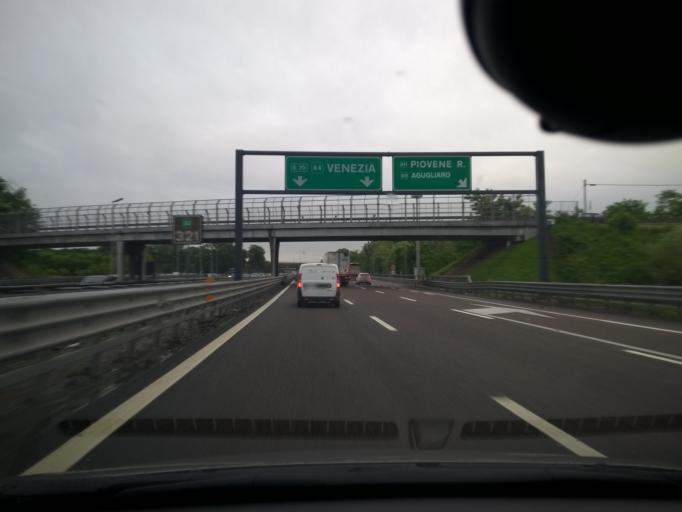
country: IT
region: Veneto
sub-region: Provincia di Vicenza
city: Torri di Quartesolo
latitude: 45.5085
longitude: 11.6119
